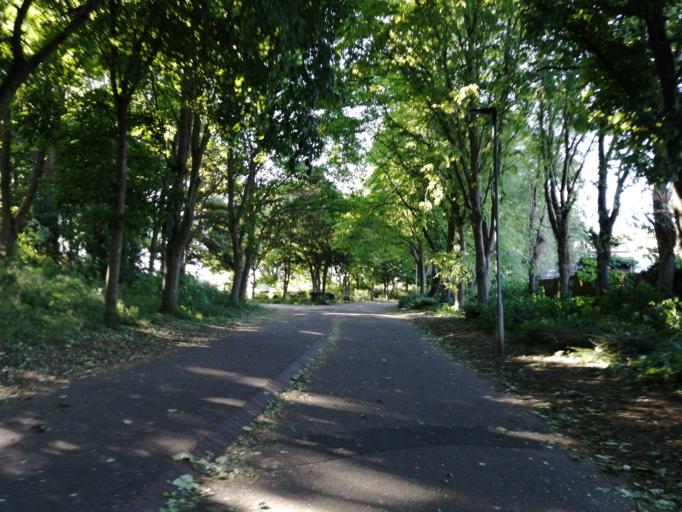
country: GB
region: England
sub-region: Peterborough
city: Marholm
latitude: 52.5986
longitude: -0.2789
